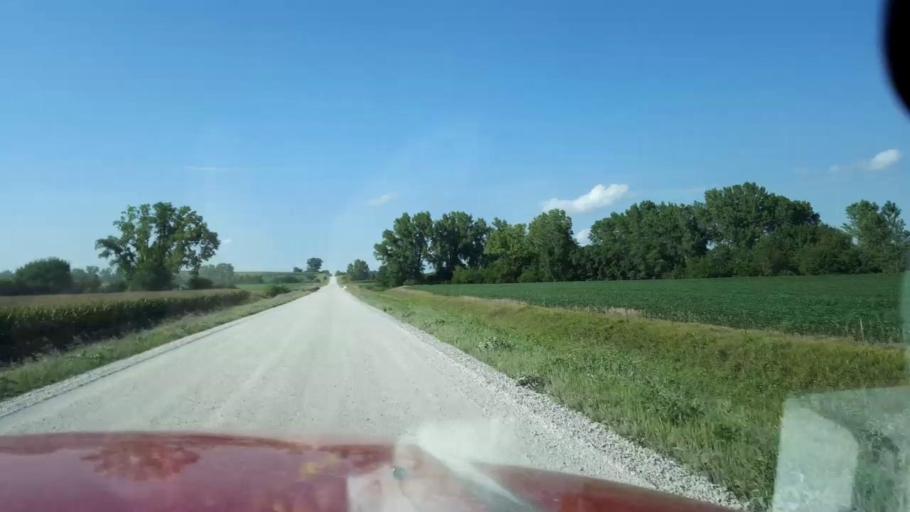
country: US
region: Iowa
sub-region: Pottawattamie County
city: Oakland
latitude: 41.2473
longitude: -95.5371
